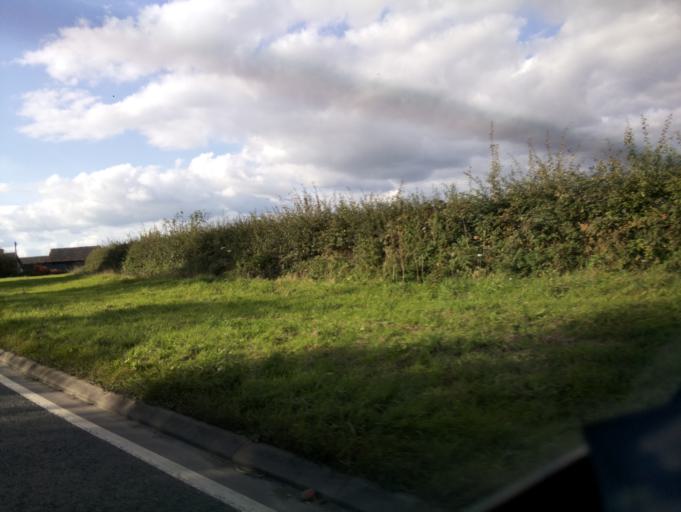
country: GB
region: England
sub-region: Herefordshire
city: Kinnersley
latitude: 52.1213
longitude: -2.9988
